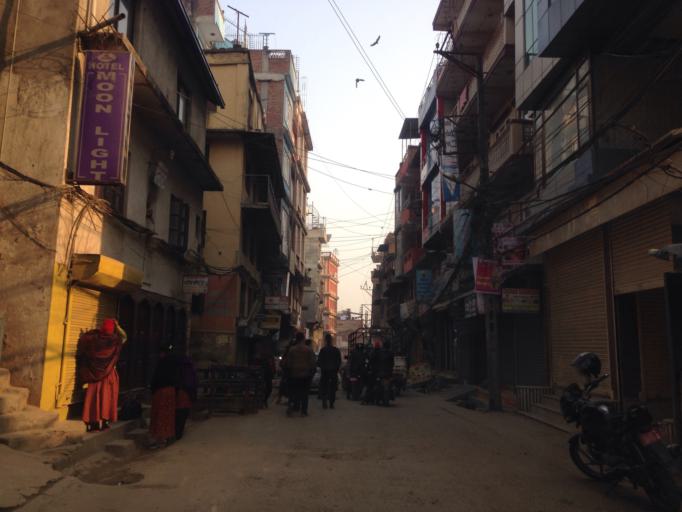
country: NP
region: Central Region
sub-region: Bagmati Zone
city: Kathmandu
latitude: 27.7167
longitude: 85.3088
